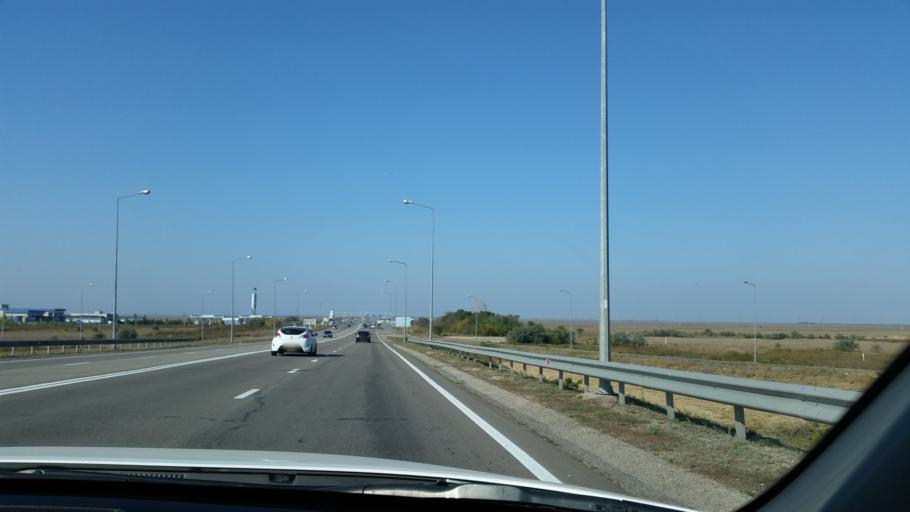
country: KZ
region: Astana Qalasy
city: Astana
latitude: 51.2574
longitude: 71.3734
